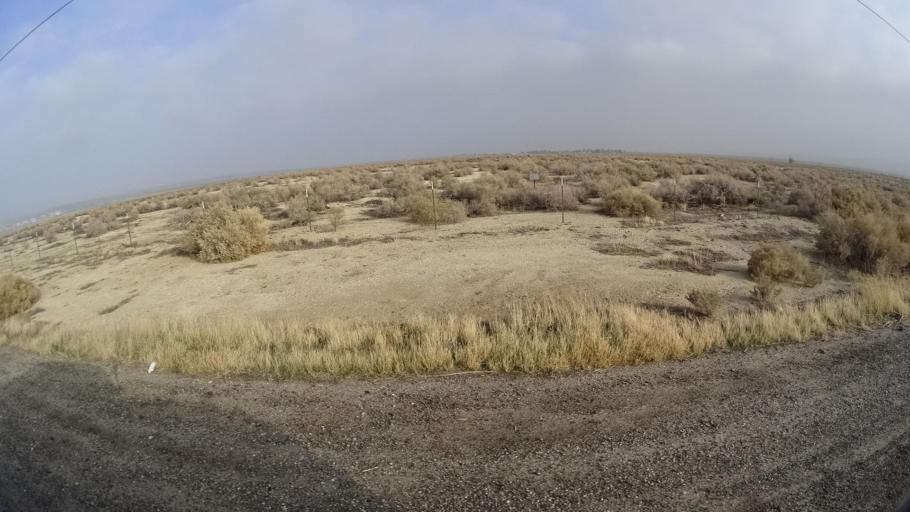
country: US
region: California
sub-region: Kern County
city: Ford City
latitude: 35.2156
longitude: -119.4456
